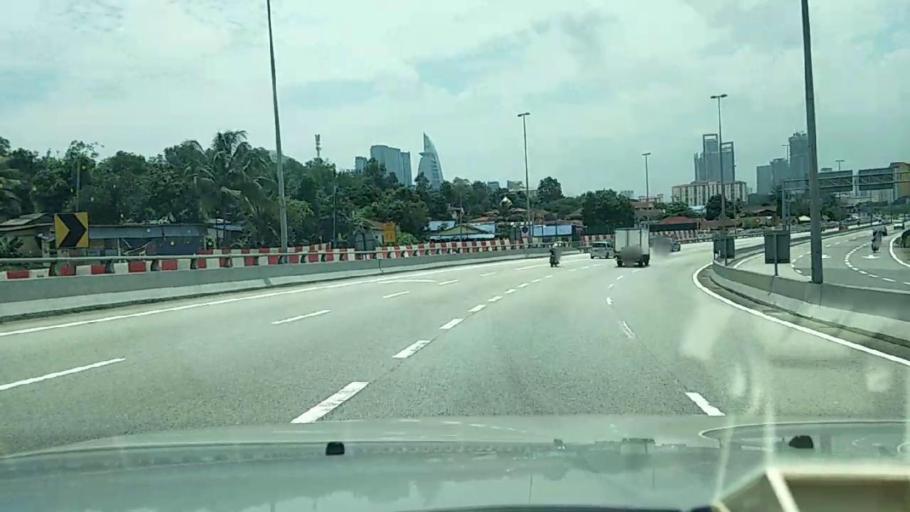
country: MY
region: Kuala Lumpur
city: Kuala Lumpur
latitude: 3.0955
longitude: 101.6693
